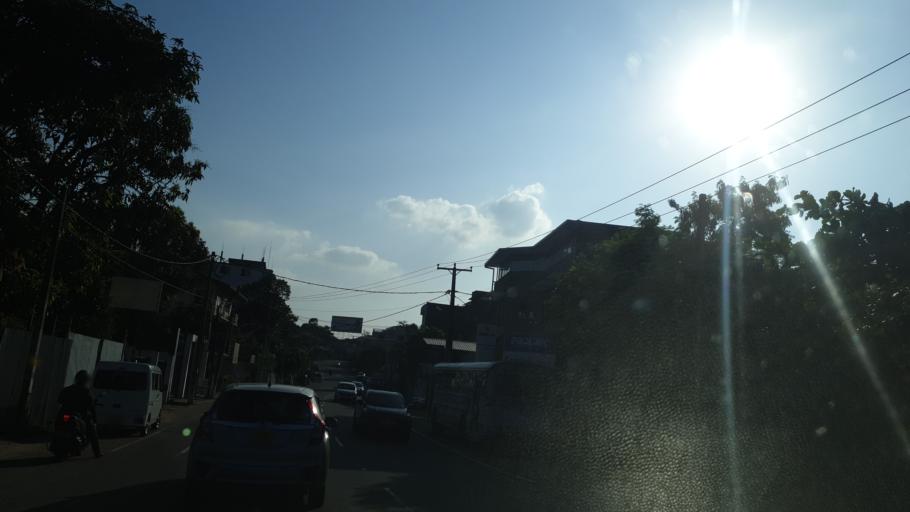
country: LK
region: Western
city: Sri Jayewardenepura Kotte
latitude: 6.8586
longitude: 79.8939
